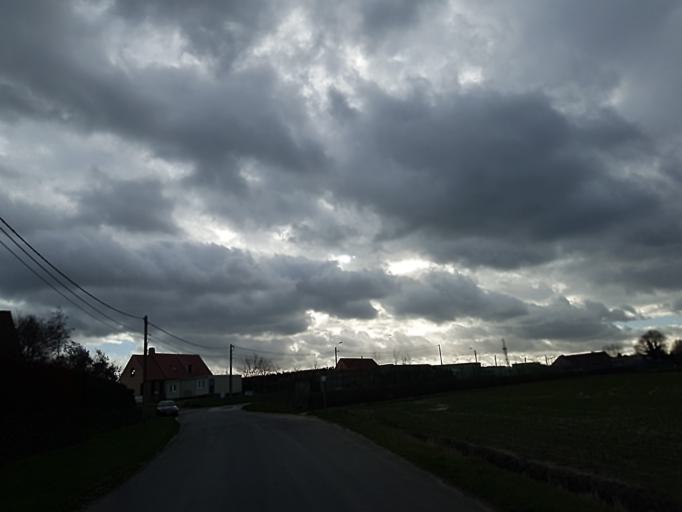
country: BE
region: Flanders
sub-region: Provincie Oost-Vlaanderen
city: Kruishoutem
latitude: 50.9037
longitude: 3.5357
